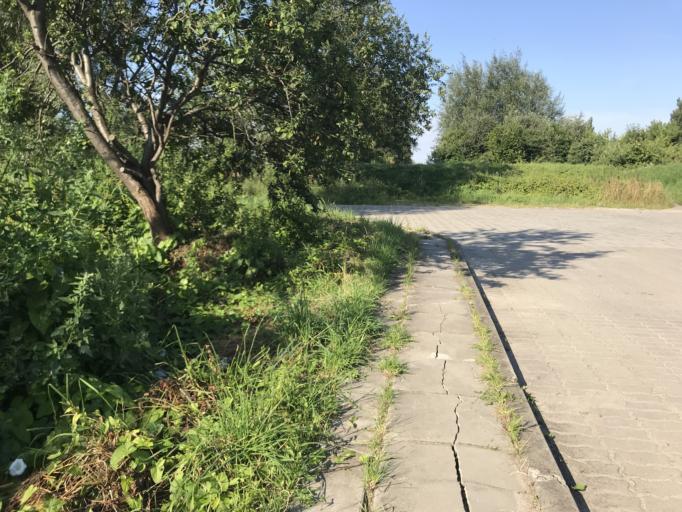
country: PL
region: Pomeranian Voivodeship
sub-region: Gdansk
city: Gdansk
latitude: 54.3442
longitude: 18.6747
